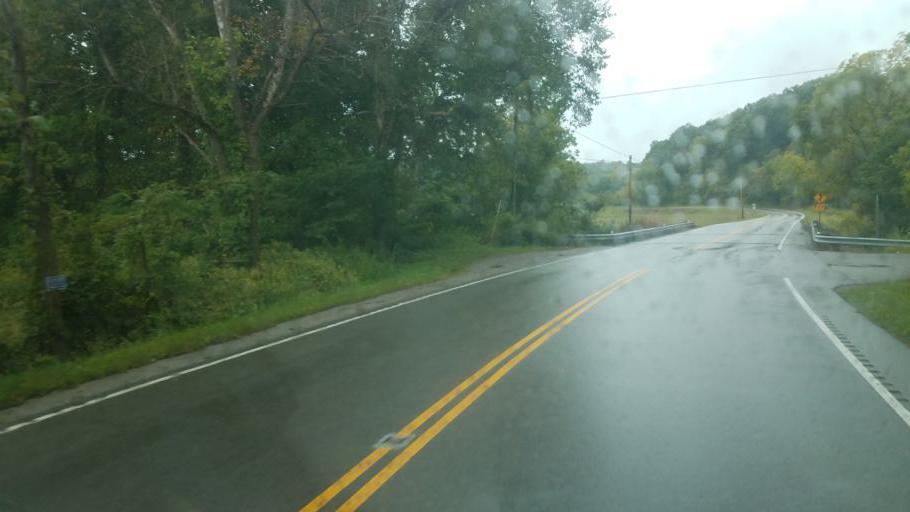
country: US
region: Ohio
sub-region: Jackson County
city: Oak Hill
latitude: 38.8197
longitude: -82.6711
